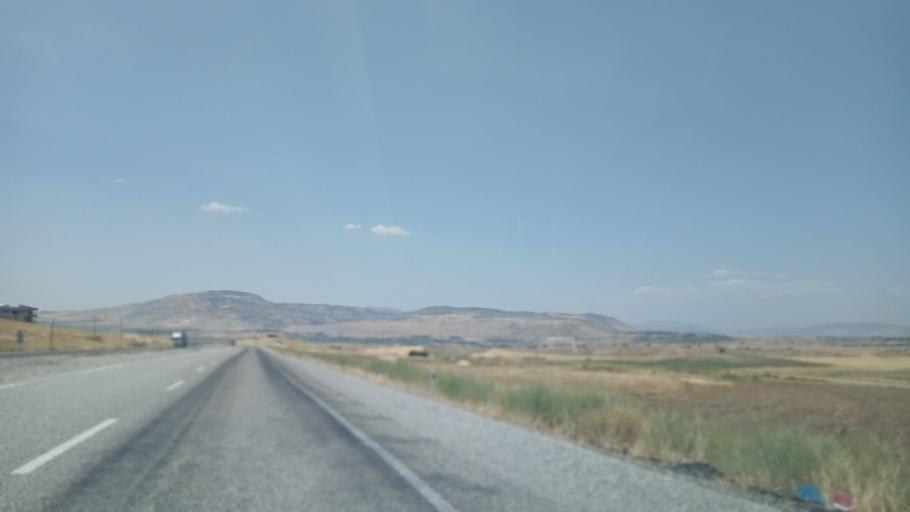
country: TR
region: Batman
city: Bekirhan
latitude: 38.1355
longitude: 41.2594
